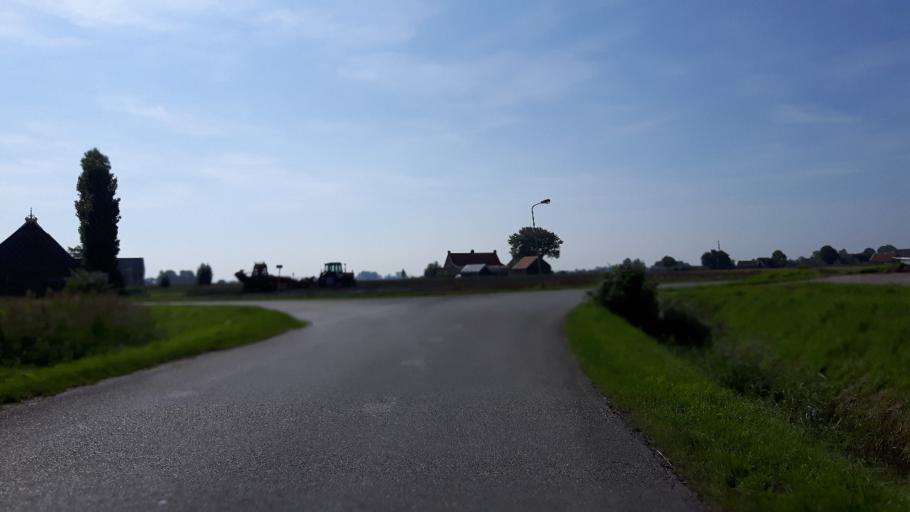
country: NL
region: Friesland
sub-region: Gemeente Dongeradeel
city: Holwerd
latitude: 53.3565
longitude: 5.8703
